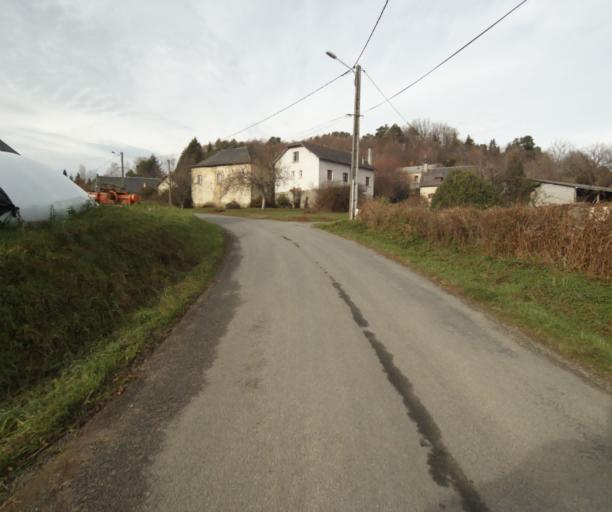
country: FR
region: Limousin
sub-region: Departement de la Correze
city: Chameyrat
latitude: 45.2559
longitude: 1.7002
